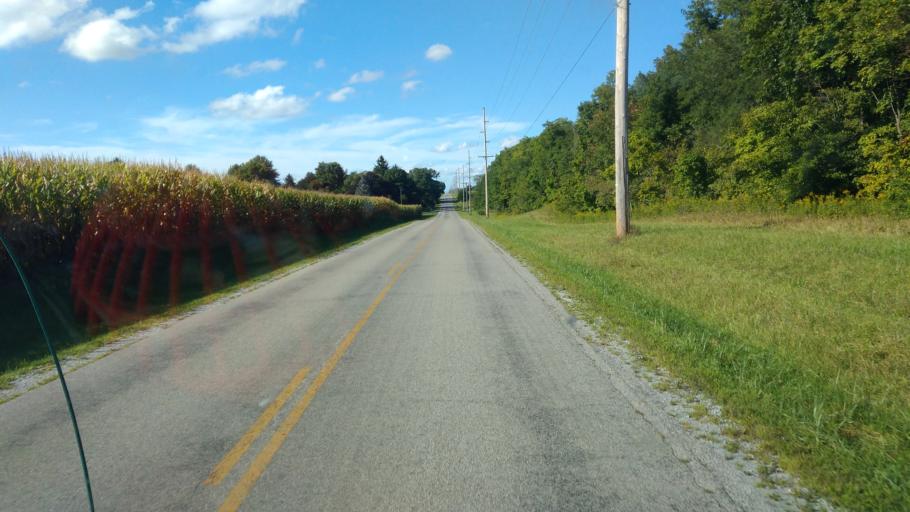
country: US
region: Ohio
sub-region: Hardin County
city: Kenton
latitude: 40.7129
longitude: -83.6533
